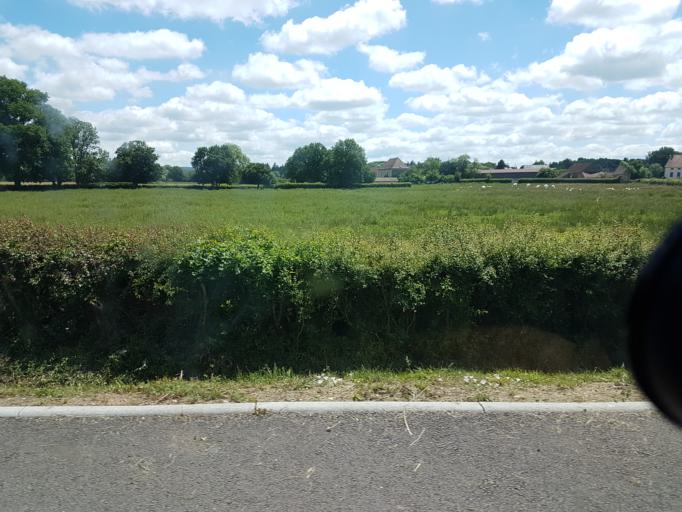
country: FR
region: Bourgogne
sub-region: Departement de Saone-et-Loire
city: Curgy
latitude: 47.0146
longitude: 4.4466
